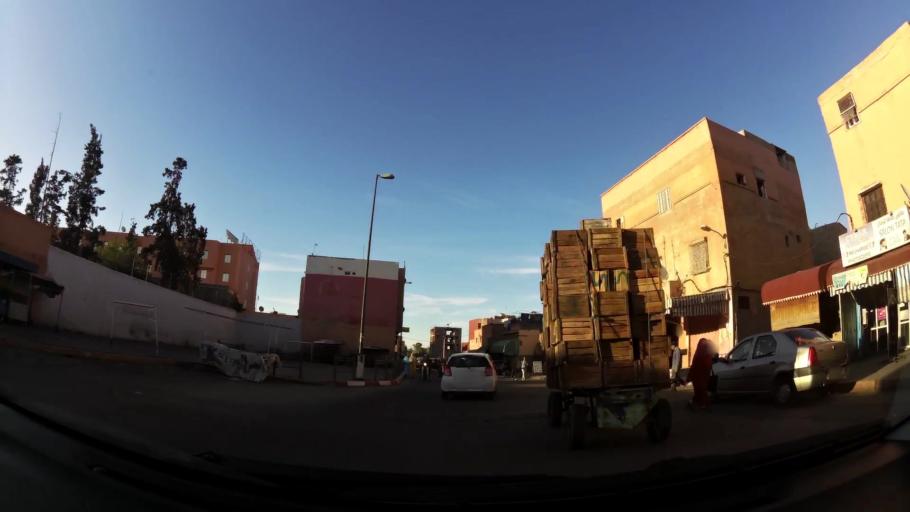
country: MA
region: Marrakech-Tensift-Al Haouz
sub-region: Marrakech
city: Marrakesh
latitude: 31.6265
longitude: -8.0428
